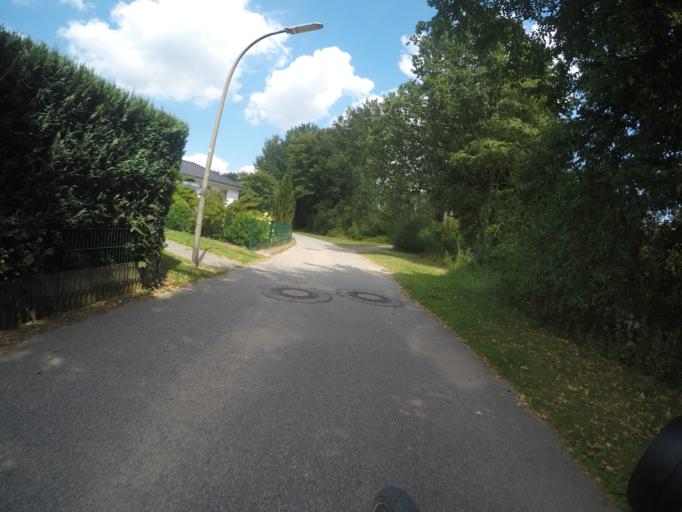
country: DE
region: Hamburg
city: Bergedorf
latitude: 53.5084
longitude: 10.2032
